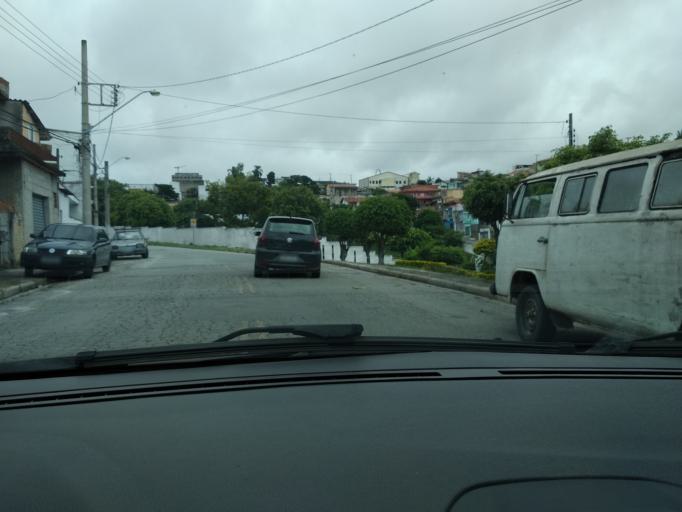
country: BR
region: Sao Paulo
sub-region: Mogi das Cruzes
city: Mogi das Cruzes
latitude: -23.5359
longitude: -46.1809
